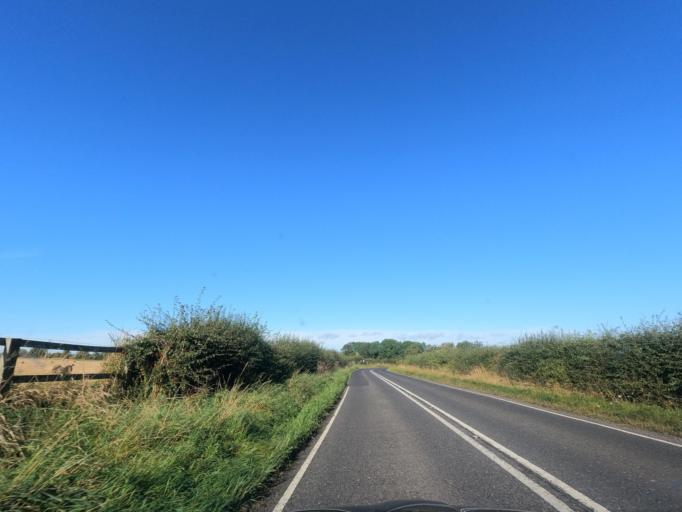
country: GB
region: England
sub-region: Northumberland
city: Ancroft
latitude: 55.7313
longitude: -2.0932
